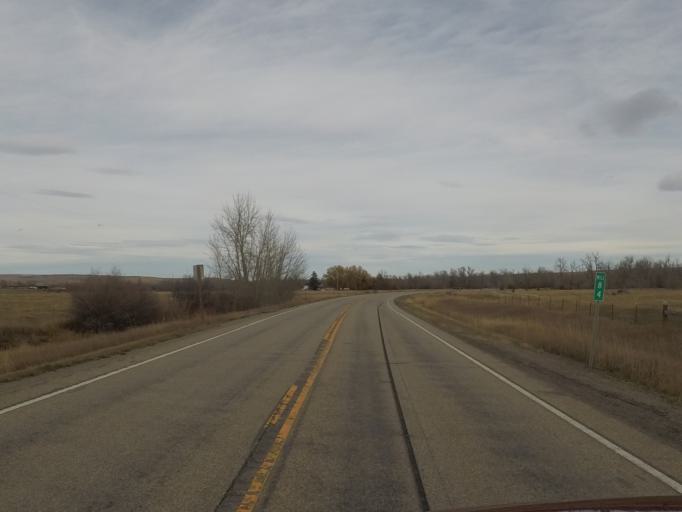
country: US
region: Montana
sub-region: Carbon County
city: Red Lodge
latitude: 45.3798
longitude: -109.1485
